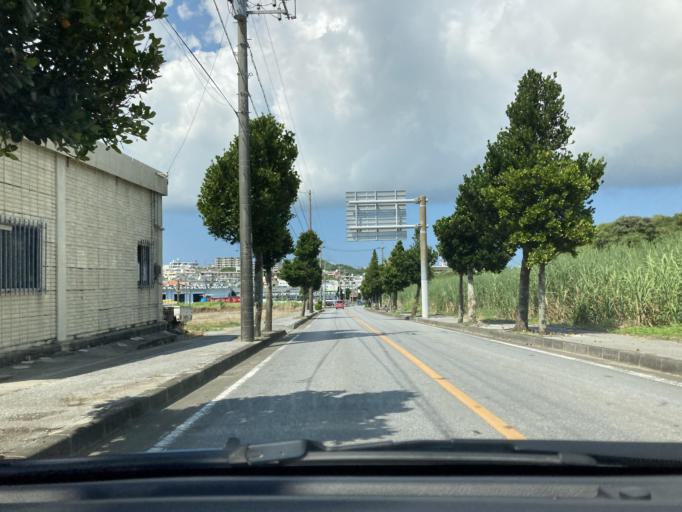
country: JP
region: Okinawa
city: Tomigusuku
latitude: 26.1744
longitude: 127.7242
